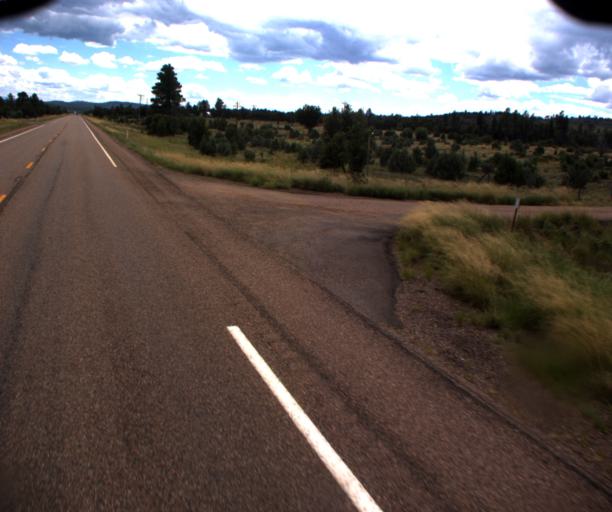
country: US
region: Arizona
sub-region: Navajo County
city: Linden
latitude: 34.3284
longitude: -110.2619
